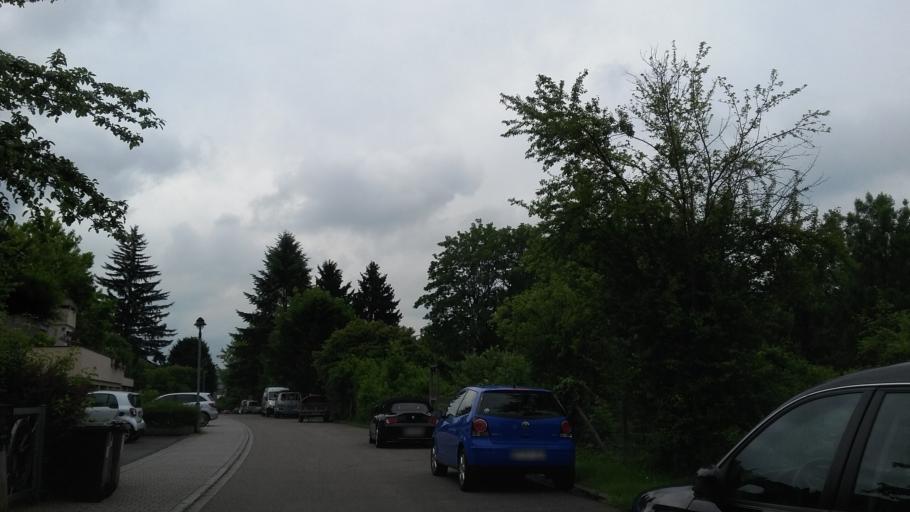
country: DE
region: Baden-Wuerttemberg
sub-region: Regierungsbezirk Stuttgart
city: Esslingen
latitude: 48.7406
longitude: 9.3297
